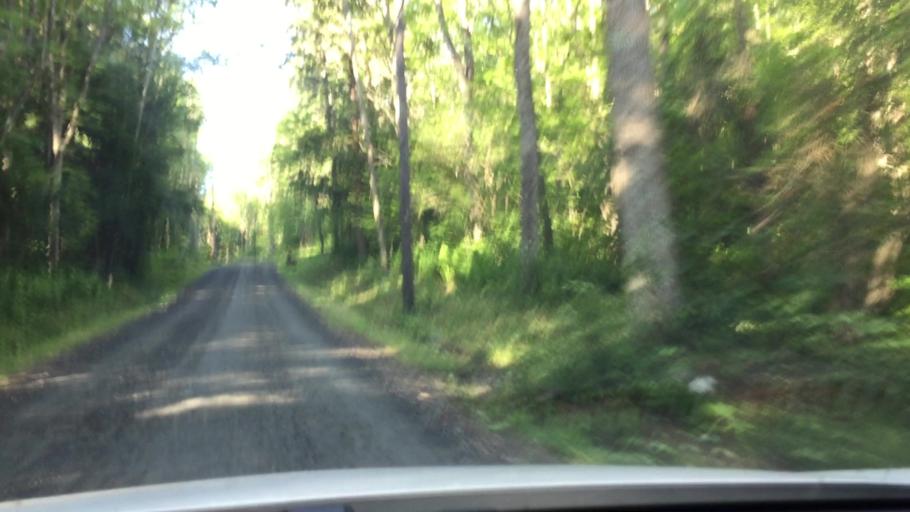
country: US
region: Massachusetts
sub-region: Berkshire County
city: Lee
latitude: 42.2691
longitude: -73.2013
